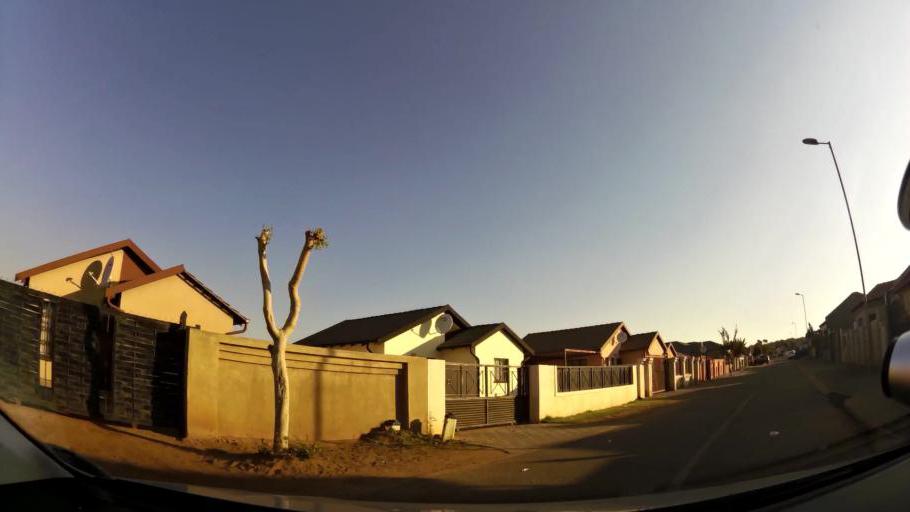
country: ZA
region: Gauteng
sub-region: City of Tshwane Metropolitan Municipality
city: Pretoria
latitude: -25.7409
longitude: 28.1151
